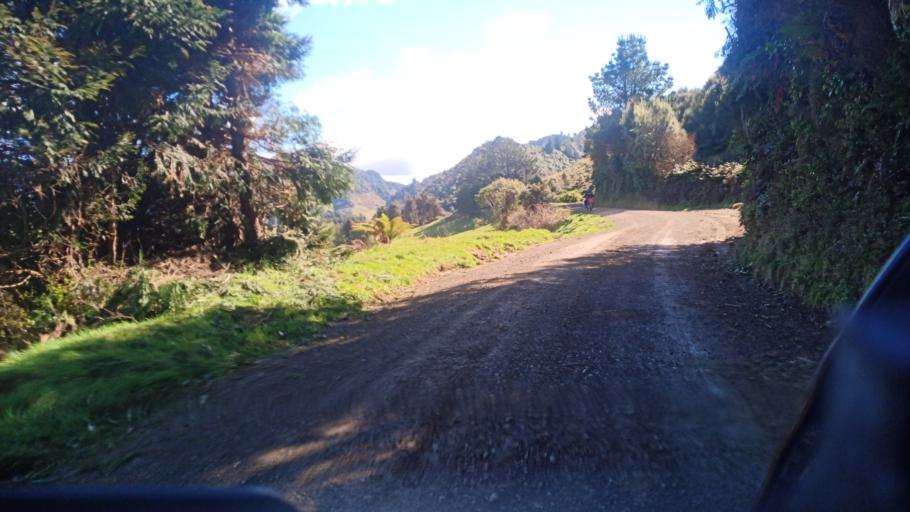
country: NZ
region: Bay of Plenty
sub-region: Opotiki District
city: Opotiki
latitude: -38.1068
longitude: 177.5007
